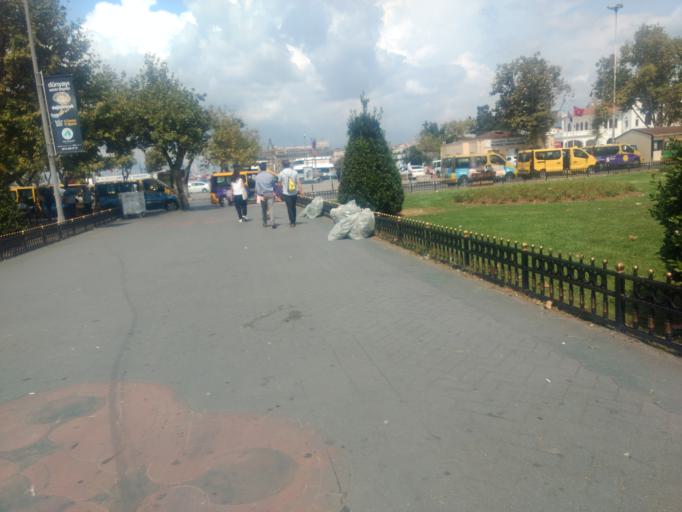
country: TR
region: Istanbul
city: UEskuedar
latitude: 40.9904
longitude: 29.0213
